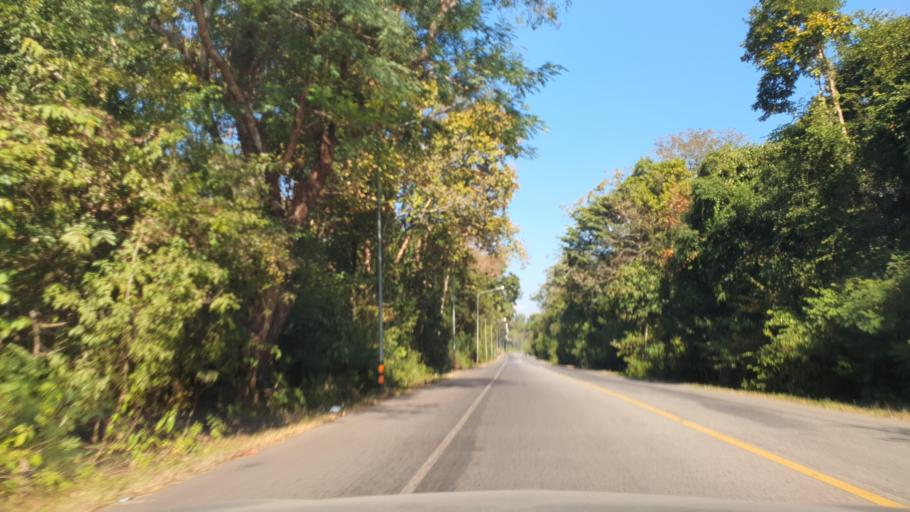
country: TH
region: Sakon Nakhon
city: Phu Phan
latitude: 17.1013
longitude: 103.9935
